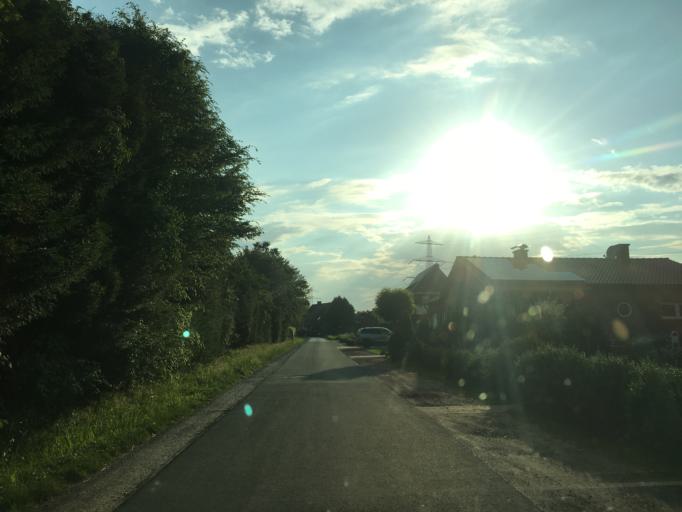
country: DE
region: North Rhine-Westphalia
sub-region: Regierungsbezirk Munster
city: Muenster
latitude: 51.9619
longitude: 7.5315
